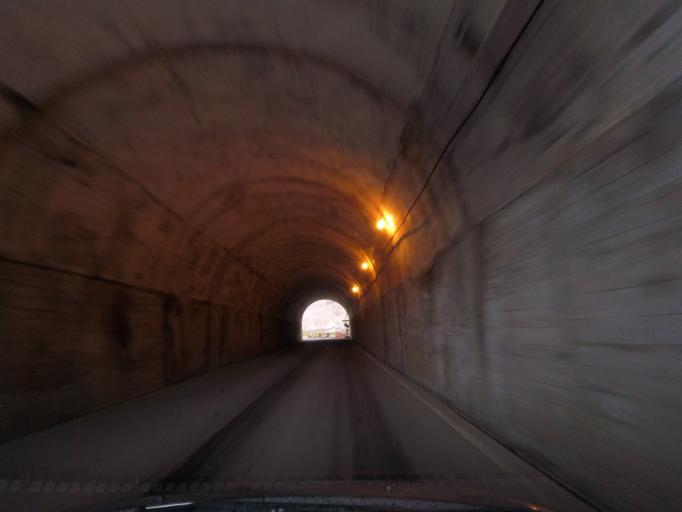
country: PT
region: Madeira
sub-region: Camara de Lobos
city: Curral das Freiras
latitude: 32.7248
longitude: -16.9665
